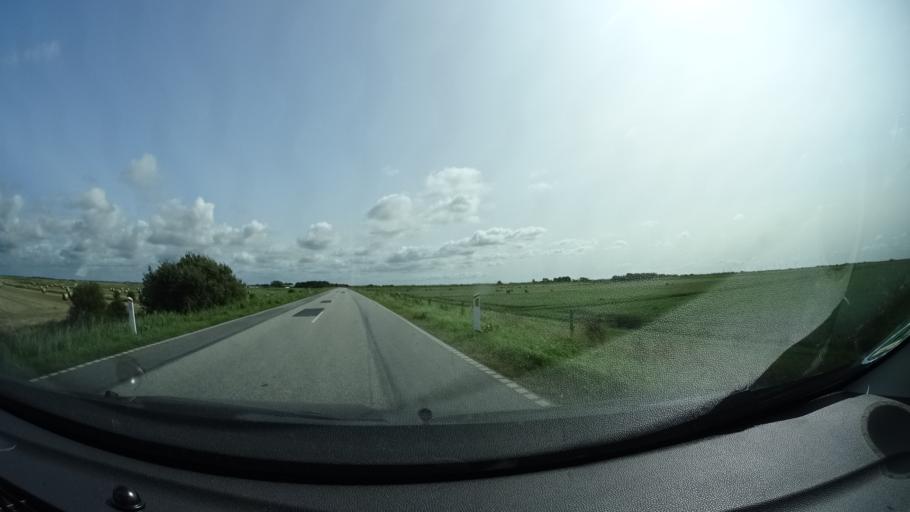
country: DE
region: Schleswig-Holstein
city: Rodenas
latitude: 54.9351
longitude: 8.7152
